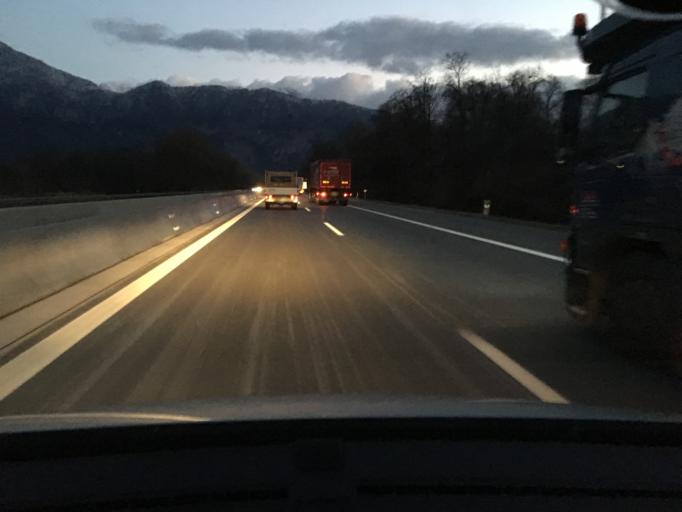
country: DE
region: Bavaria
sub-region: Upper Bavaria
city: Oberaudorf
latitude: 47.6392
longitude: 12.1938
